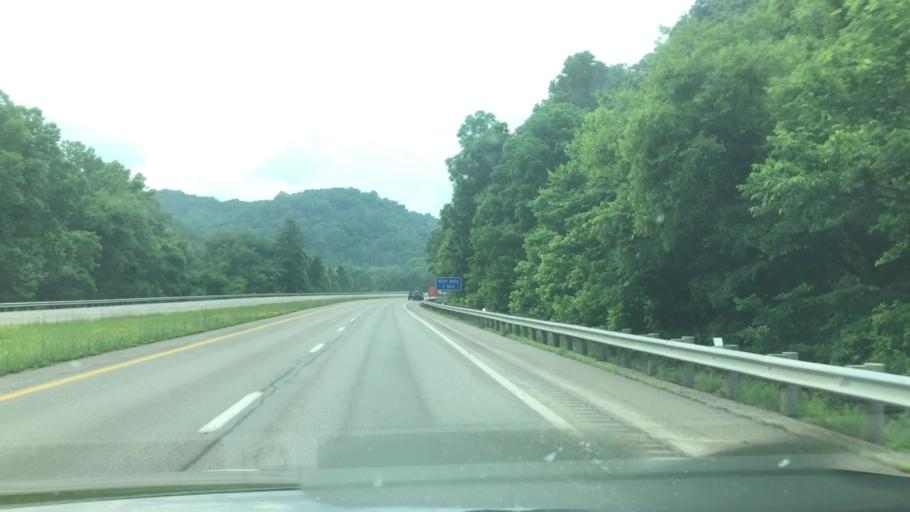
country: US
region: Ohio
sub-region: Jackson County
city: Jackson
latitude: 39.1527
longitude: -82.7303
